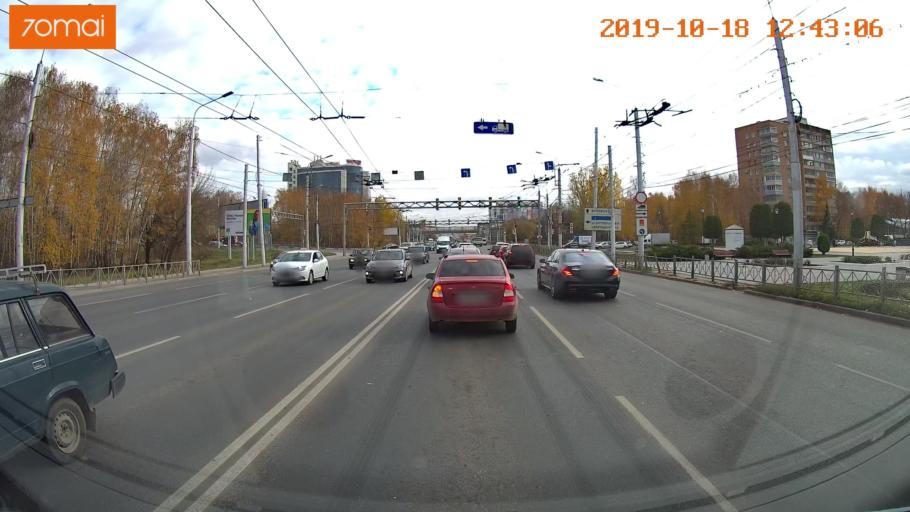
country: RU
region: Rjazan
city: Ryazan'
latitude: 54.6453
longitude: 39.6591
